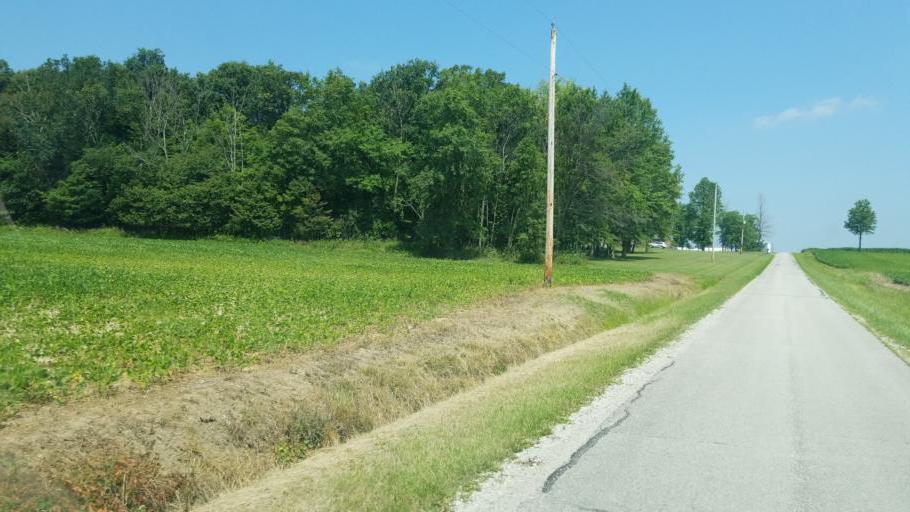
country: US
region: Ohio
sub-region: Sandusky County
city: Green Springs
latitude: 41.0863
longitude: -82.9768
